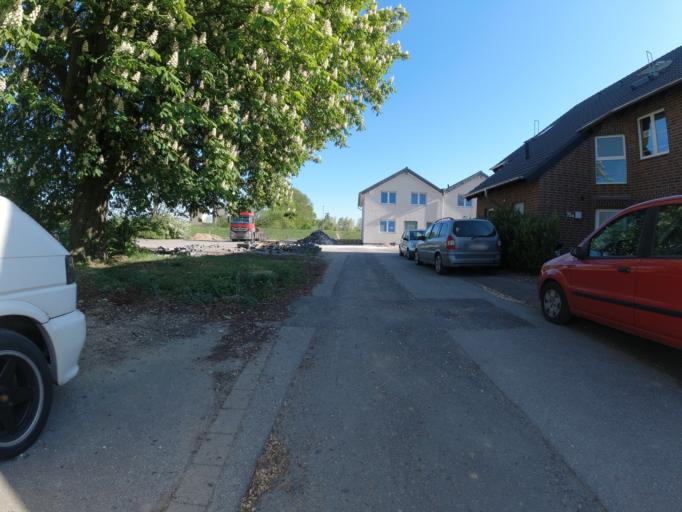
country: DE
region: North Rhine-Westphalia
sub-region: Regierungsbezirk Dusseldorf
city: Hochfeld
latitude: 51.3838
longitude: 6.7116
